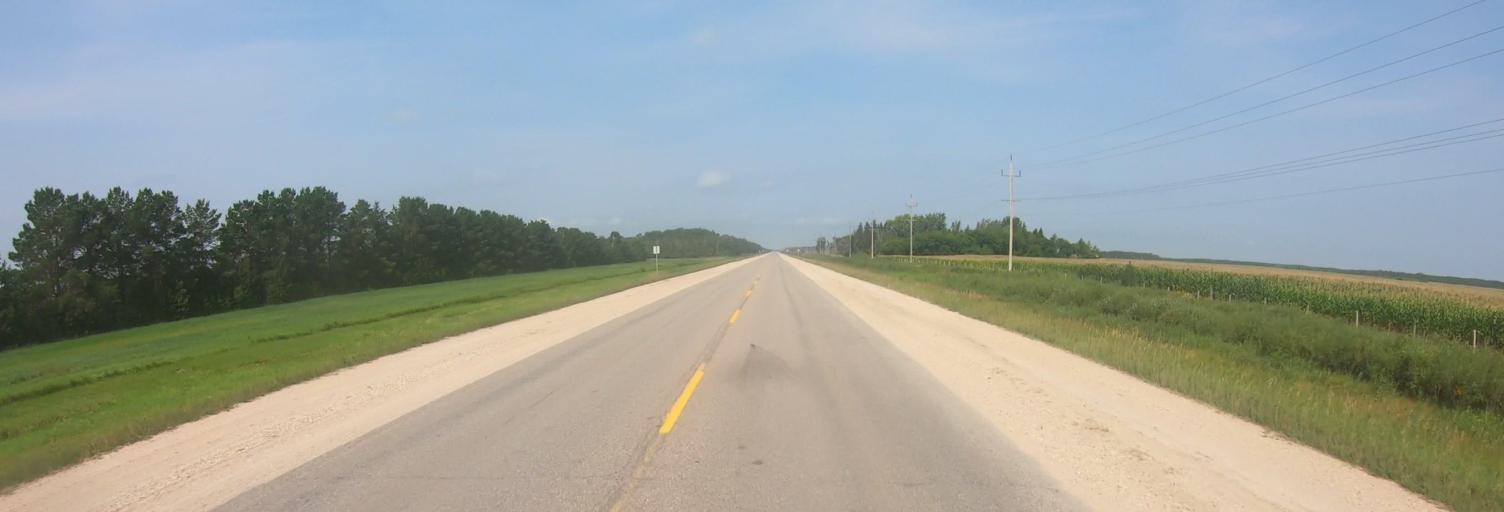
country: CA
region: Manitoba
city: La Broquerie
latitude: 49.3239
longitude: -96.5948
